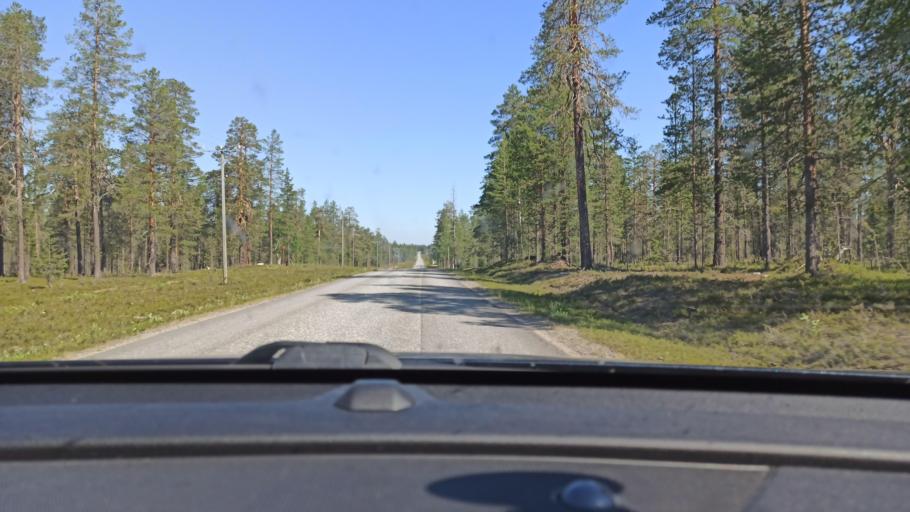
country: FI
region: Lapland
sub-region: Tunturi-Lappi
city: Kolari
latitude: 67.6423
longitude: 24.1585
